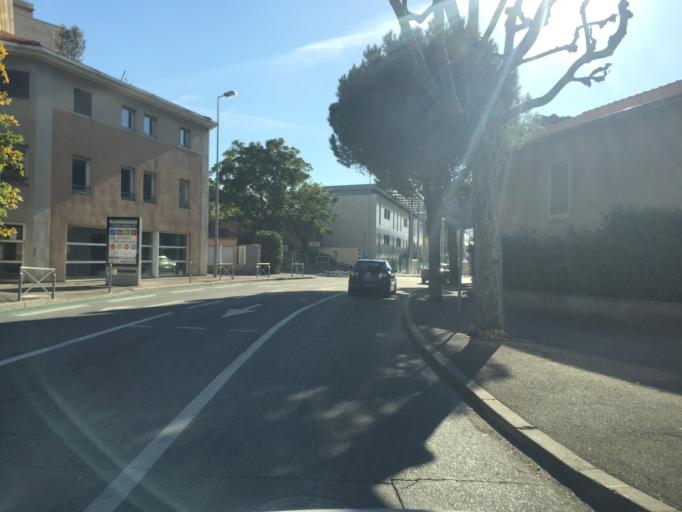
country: FR
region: Provence-Alpes-Cote d'Azur
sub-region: Departement des Bouches-du-Rhone
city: Salon-de-Provence
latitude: 43.6413
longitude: 5.1030
